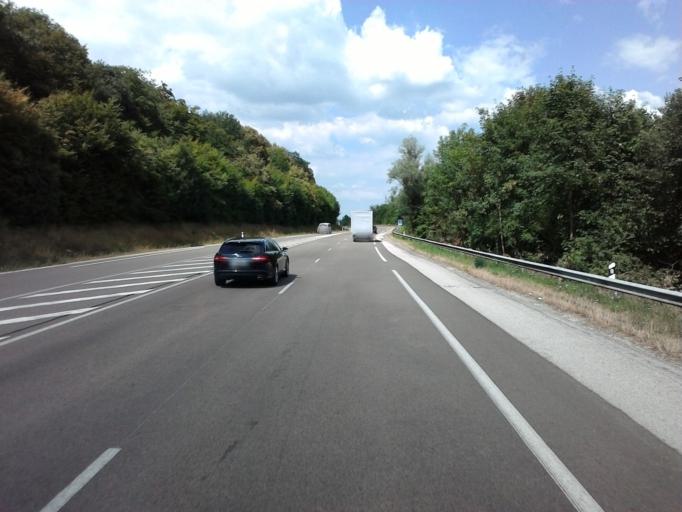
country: FR
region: Franche-Comte
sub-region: Departement du Doubs
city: Montferrand-le-Chateau
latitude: 47.1617
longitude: 5.9531
